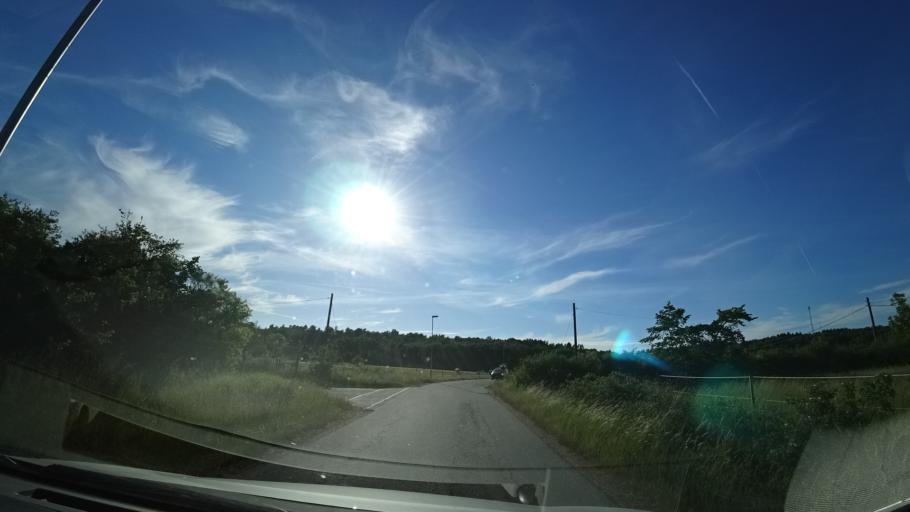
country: SE
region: Vaestra Goetaland
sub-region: Goteborg
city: Billdal
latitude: 57.5834
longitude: 11.9781
